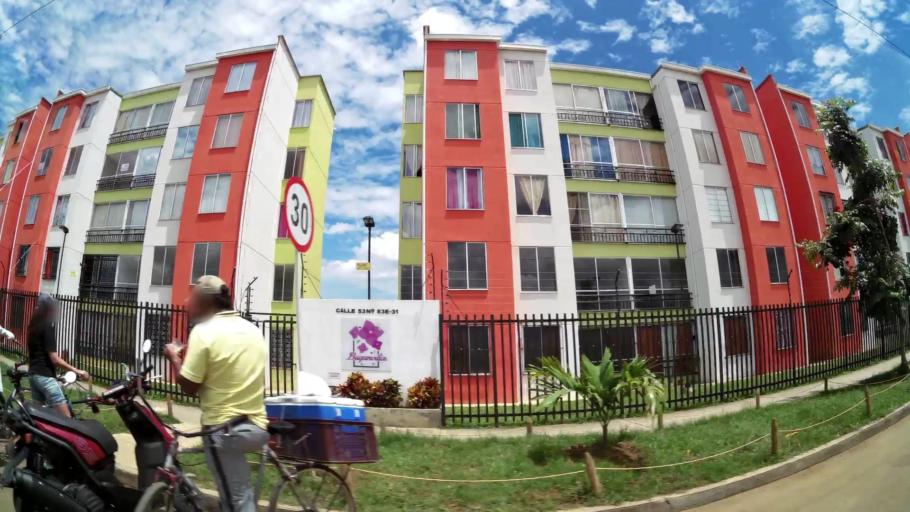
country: CO
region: Valle del Cauca
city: Cali
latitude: 3.3828
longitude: -76.5116
